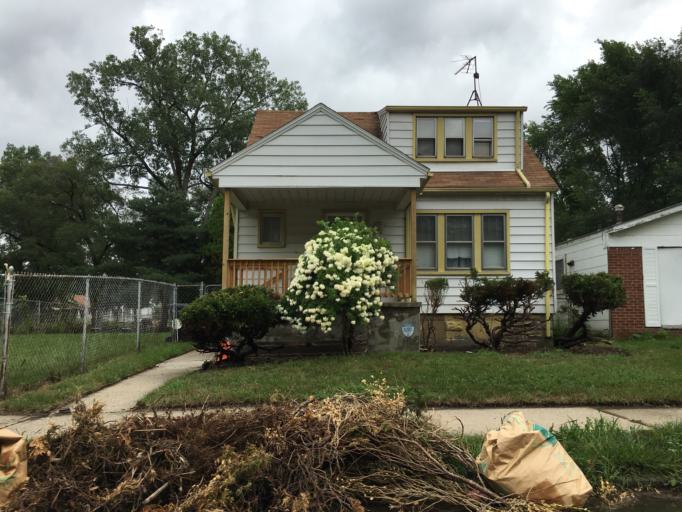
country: US
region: Michigan
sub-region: Wayne County
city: Highland Park
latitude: 42.4123
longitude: -83.1460
